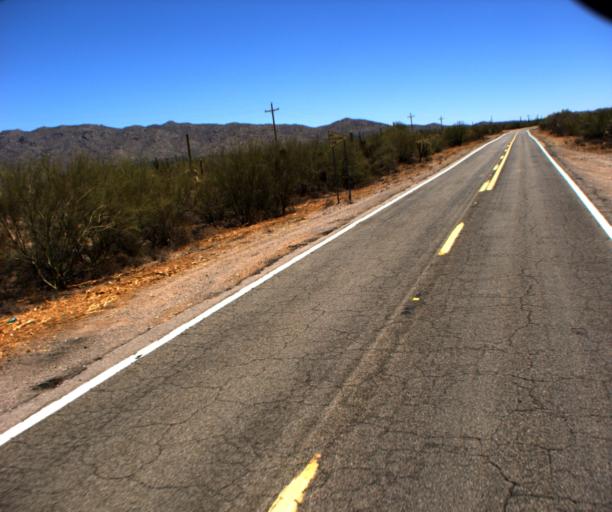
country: US
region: Arizona
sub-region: Pima County
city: Sells
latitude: 32.1821
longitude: -112.2849
